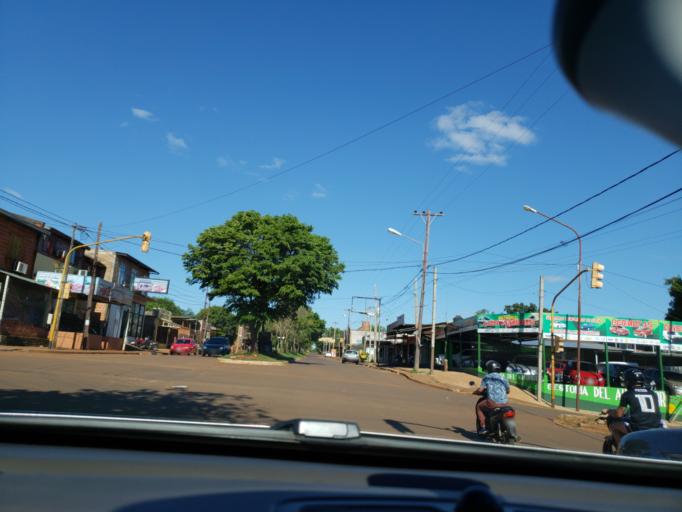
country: AR
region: Misiones
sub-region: Departamento de Capital
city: Posadas
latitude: -27.3831
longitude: -55.9418
